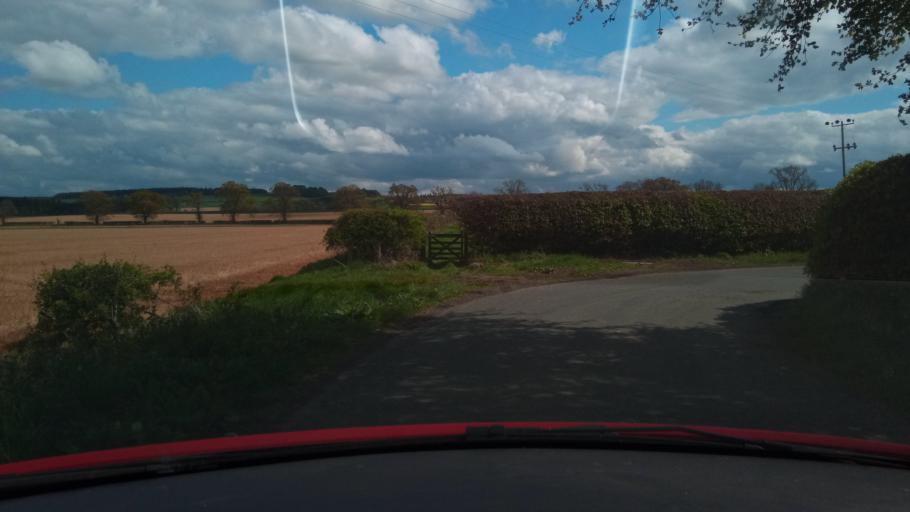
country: GB
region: Scotland
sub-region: The Scottish Borders
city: Saint Boswells
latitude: 55.5608
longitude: -2.6158
